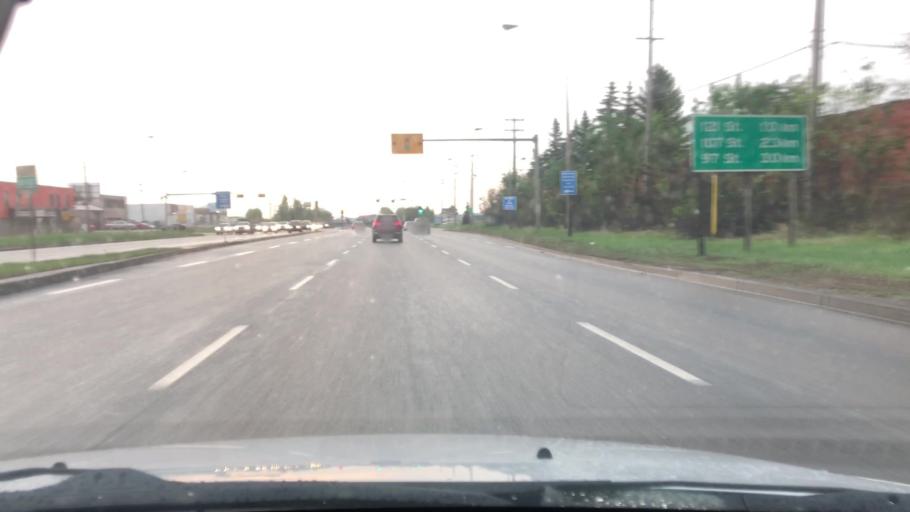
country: CA
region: Alberta
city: Edmonton
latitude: 53.5805
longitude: -113.5382
